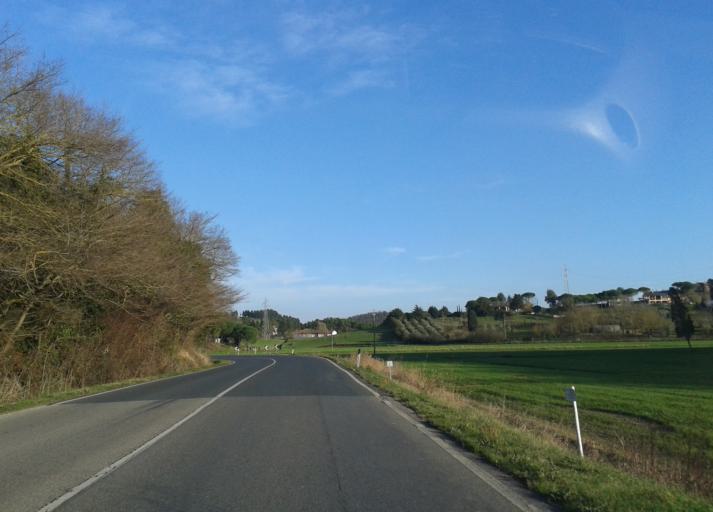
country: IT
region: Tuscany
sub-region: Provincia di Livorno
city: Guasticce
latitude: 43.5695
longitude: 10.4258
